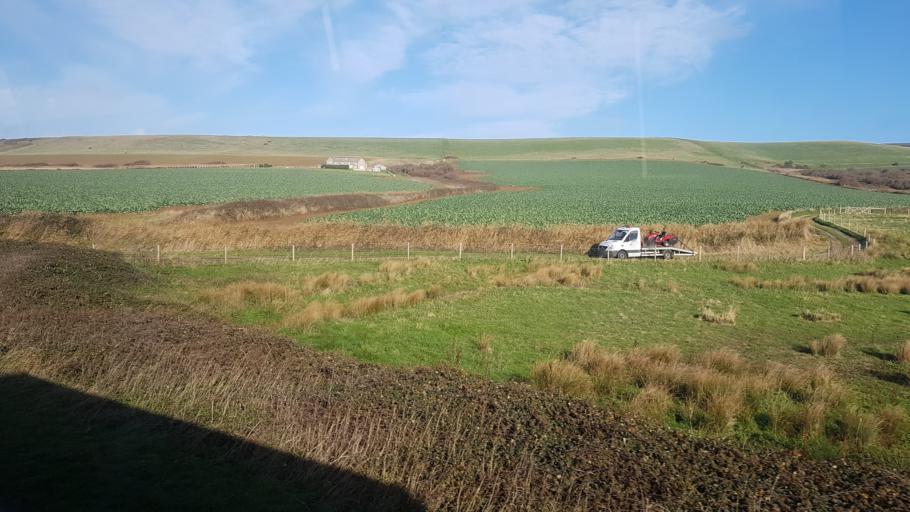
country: GB
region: England
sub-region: Isle of Wight
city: Freshwater
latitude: 50.6552
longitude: -1.4661
